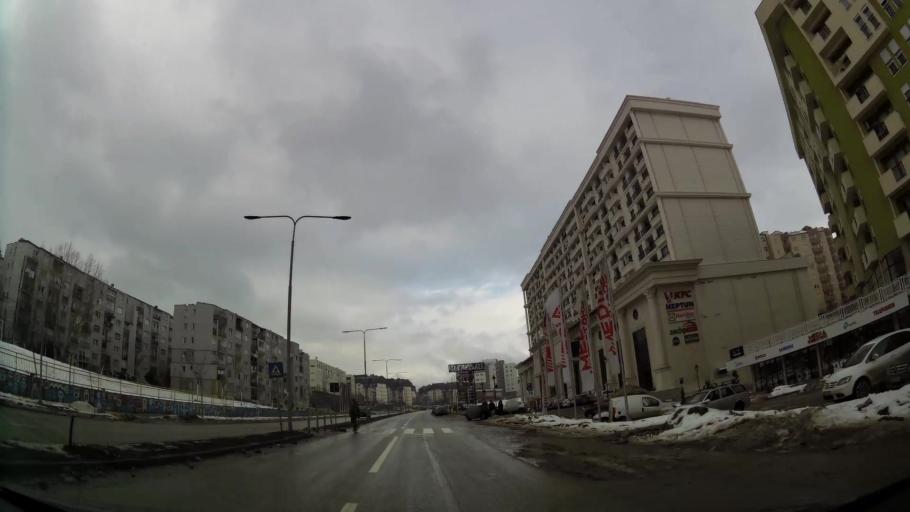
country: XK
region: Pristina
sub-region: Komuna e Prishtines
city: Pristina
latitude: 42.6534
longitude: 21.1764
